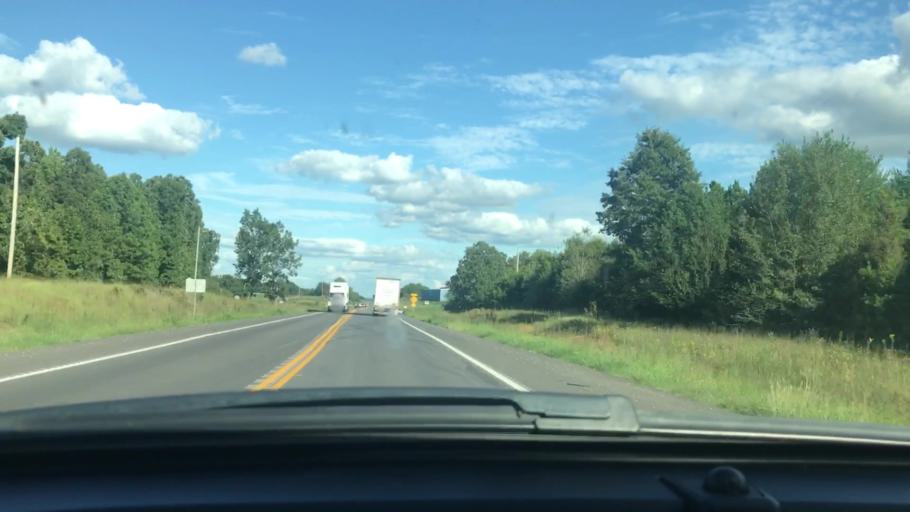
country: US
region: Missouri
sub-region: Oregon County
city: Thayer
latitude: 36.5887
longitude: -91.6382
